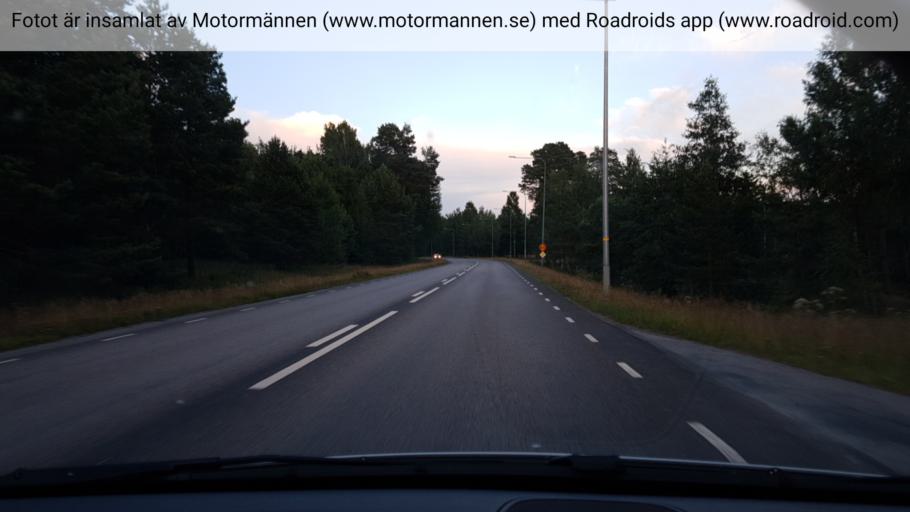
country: SE
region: Vaestra Goetaland
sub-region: Tibro Kommun
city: Tibro
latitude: 58.4114
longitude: 14.1692
